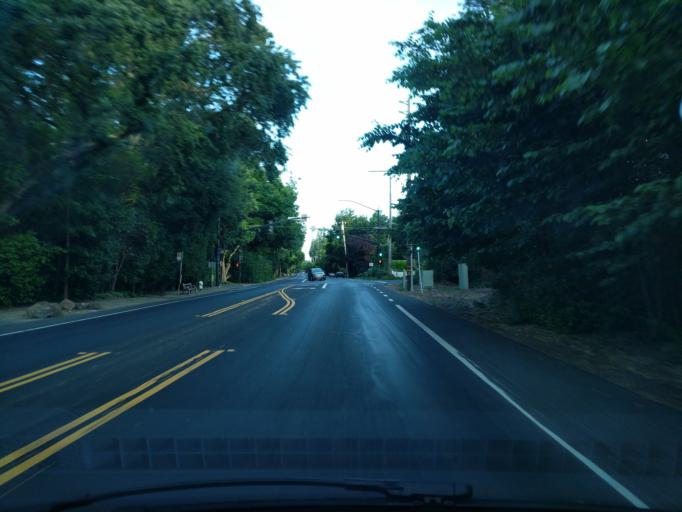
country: US
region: California
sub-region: Contra Costa County
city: Alamo
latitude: 37.8383
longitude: -122.0214
